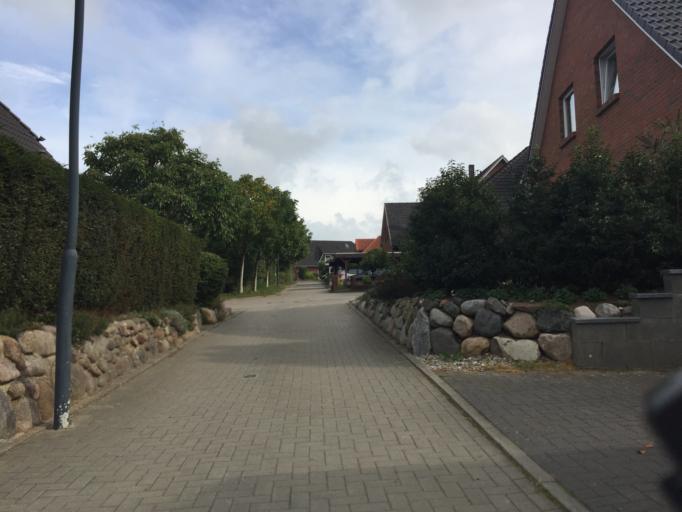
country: DE
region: Schleswig-Holstein
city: Itzehoe
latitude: 53.9330
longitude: 9.5309
